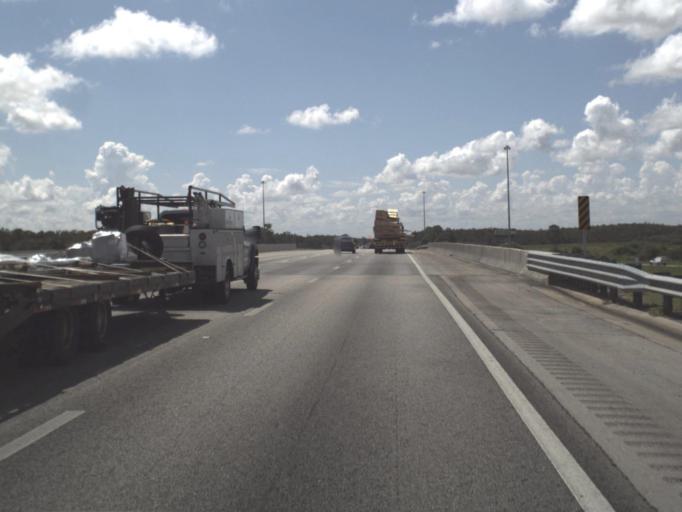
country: US
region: Florida
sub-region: Lee County
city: Fort Myers
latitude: 26.6135
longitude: -81.8036
